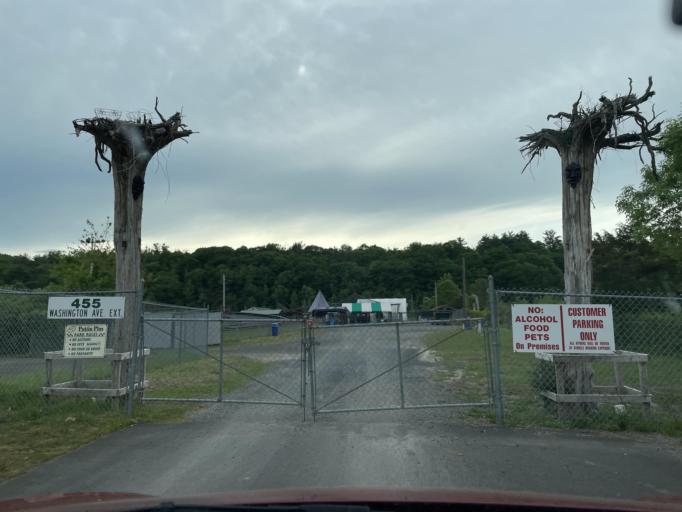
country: US
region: New York
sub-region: Ulster County
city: Saugerties
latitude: 42.0944
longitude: -73.9493
